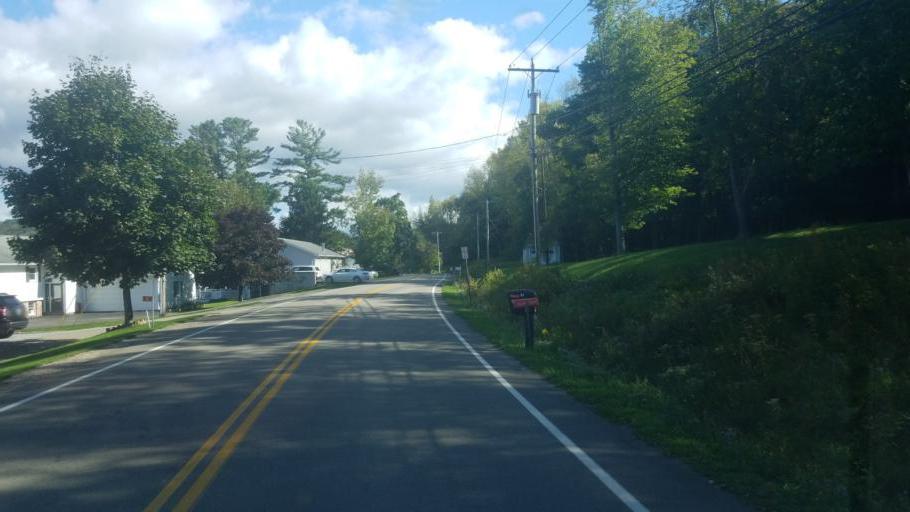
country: US
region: New York
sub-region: Allegany County
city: Cuba
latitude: 42.2441
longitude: -78.2999
